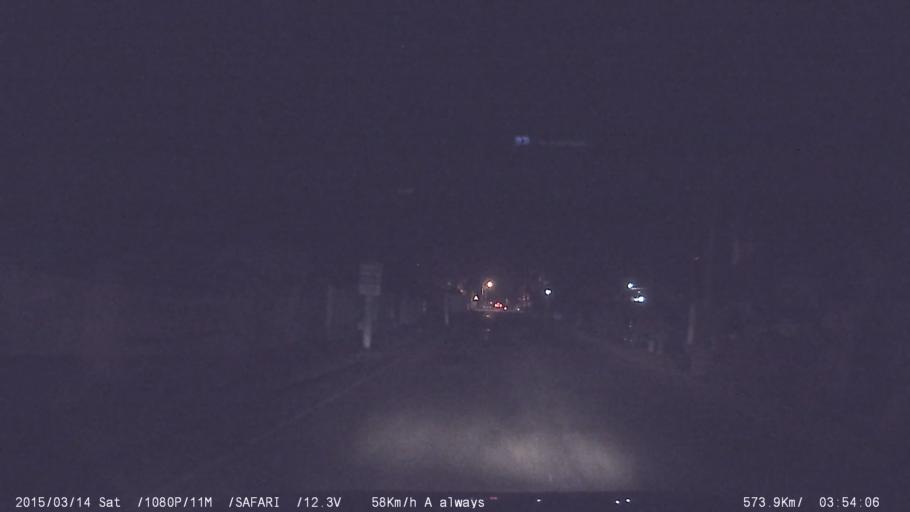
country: IN
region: Kerala
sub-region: Alappuzha
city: Alleppey
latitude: 9.4921
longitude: 76.3315
